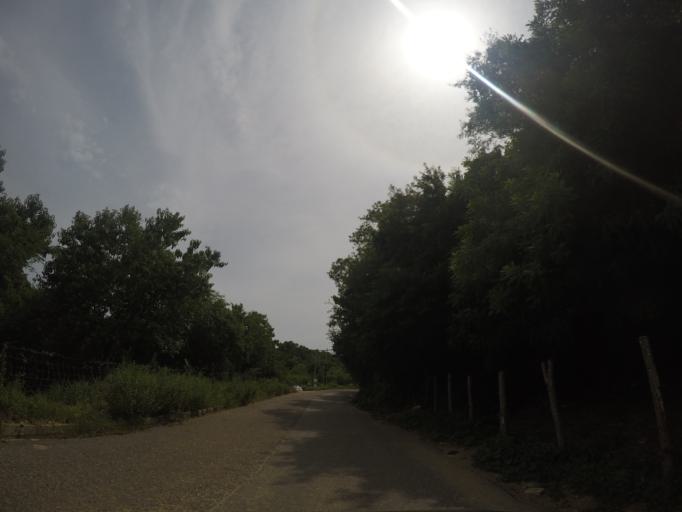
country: MX
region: Oaxaca
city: Santa Maria Tonameca
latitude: 15.6664
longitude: -96.5264
